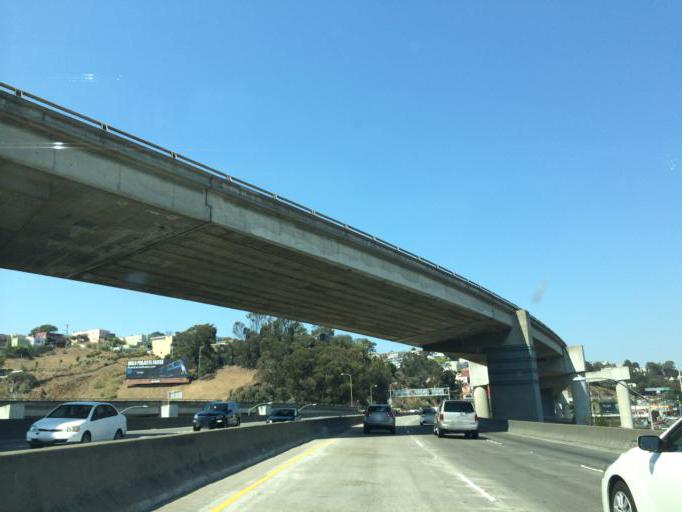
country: US
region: California
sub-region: San Francisco County
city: San Francisco
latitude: 37.7362
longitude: -122.4073
